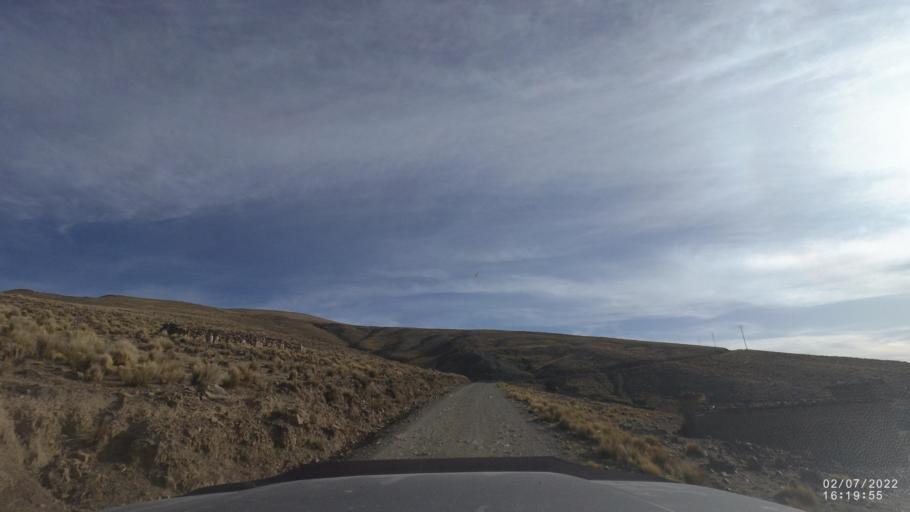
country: BO
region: Cochabamba
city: Irpa Irpa
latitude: -17.9307
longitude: -66.4454
